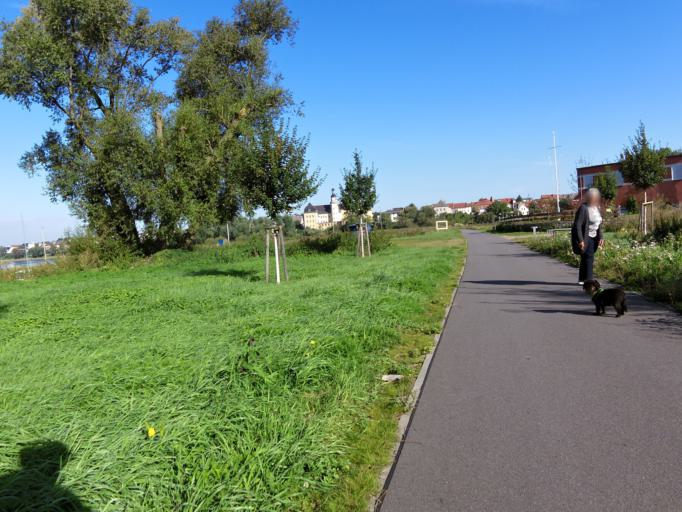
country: DE
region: Saxony-Anhalt
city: Coswig
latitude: 51.8784
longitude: 12.4547
